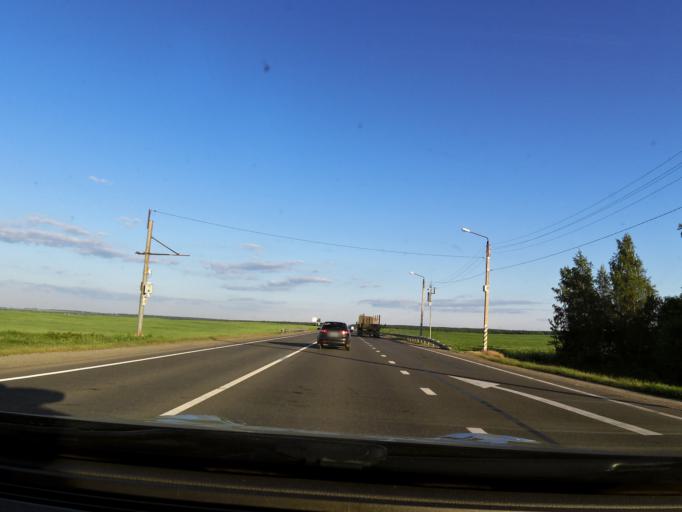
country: RU
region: Vologda
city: Vologda
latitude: 59.1536
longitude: 39.9341
